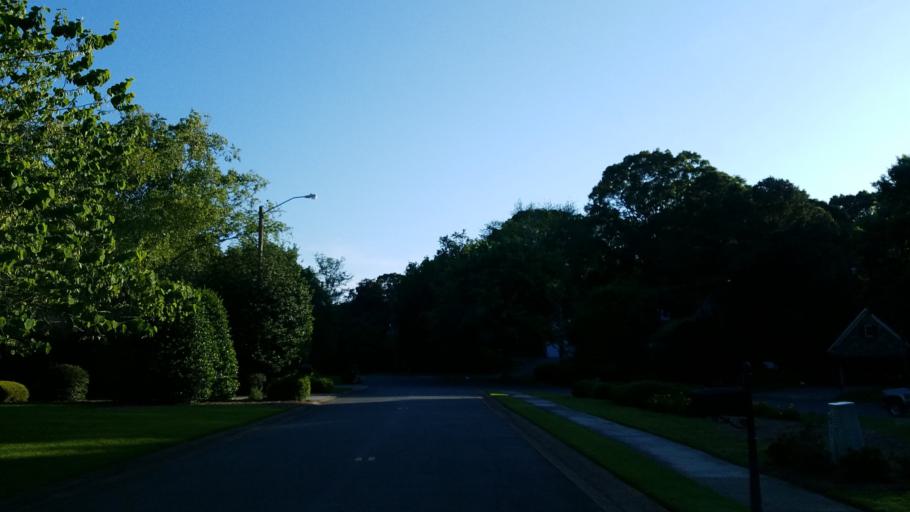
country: US
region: Georgia
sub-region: Cobb County
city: Vinings
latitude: 33.8726
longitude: -84.4868
